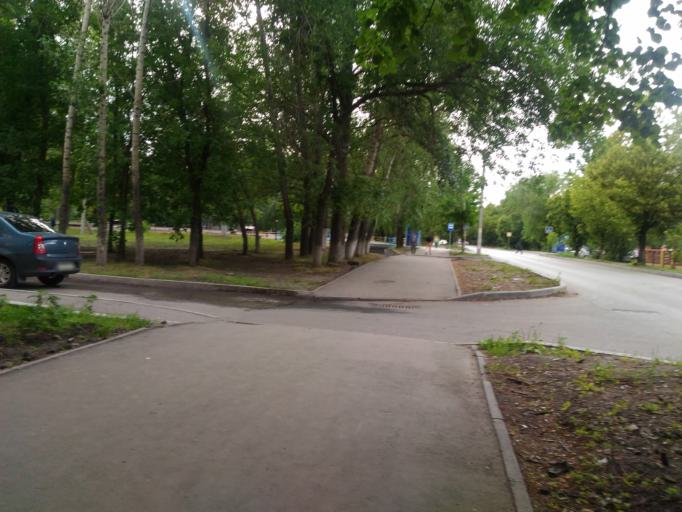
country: RU
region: Ulyanovsk
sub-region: Ulyanovskiy Rayon
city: Ulyanovsk
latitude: 54.2829
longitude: 48.2901
